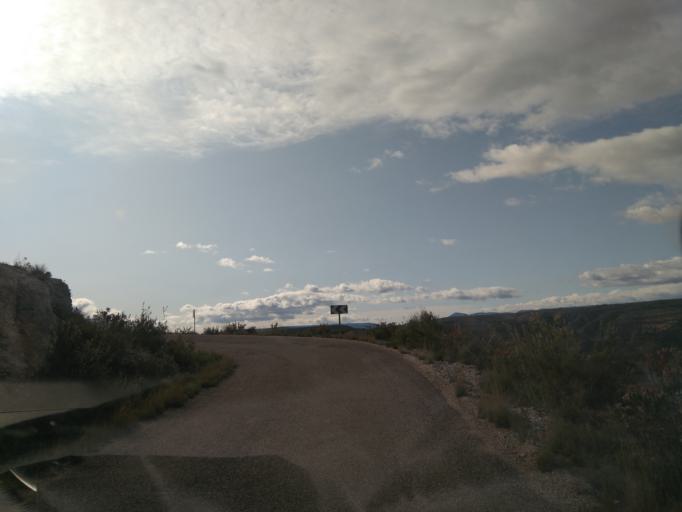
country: ES
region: Valencia
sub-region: Provincia de Valencia
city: Sumacarcer
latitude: 39.1482
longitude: -0.6477
